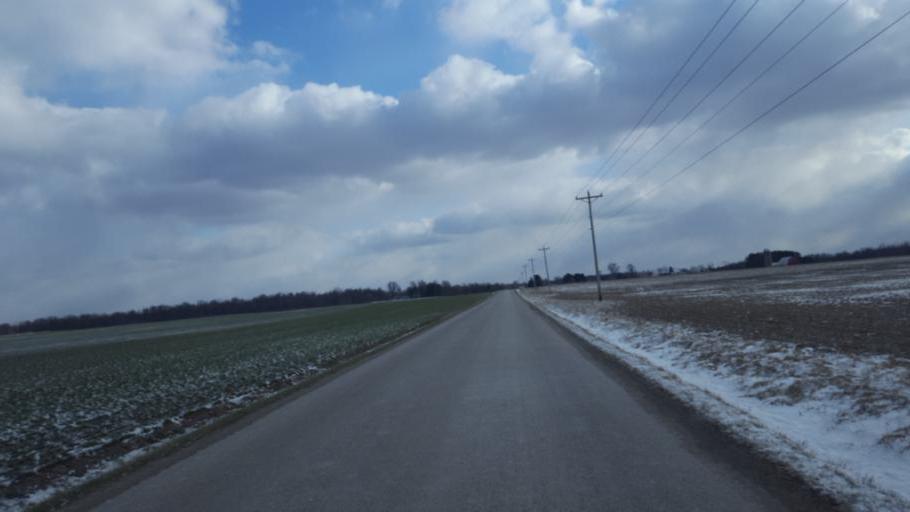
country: US
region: Ohio
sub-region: Morrow County
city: Mount Gilead
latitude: 40.5963
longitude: -82.7288
